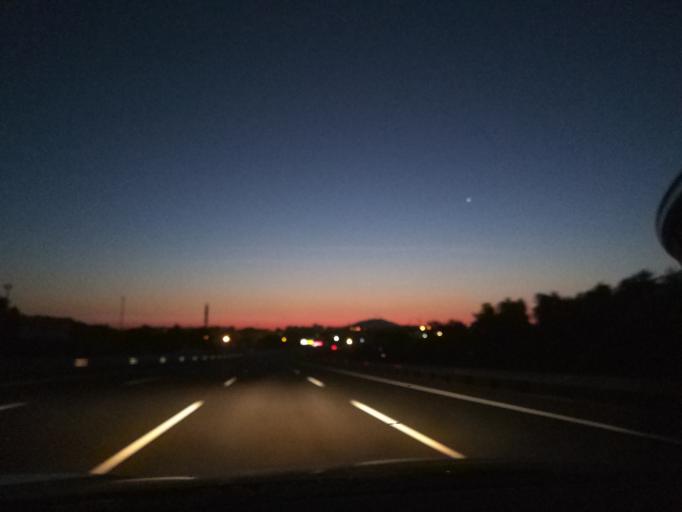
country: TR
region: Istanbul
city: Sancaktepe
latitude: 41.0456
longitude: 29.2307
